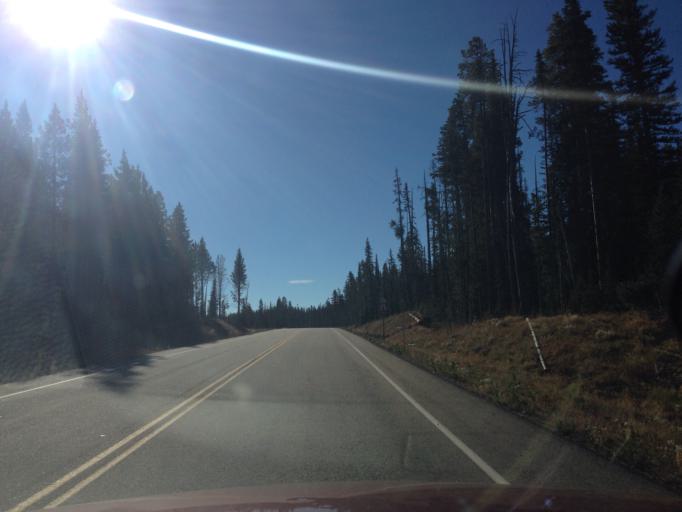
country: US
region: Montana
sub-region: Carbon County
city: Red Lodge
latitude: 45.0210
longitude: -109.8753
